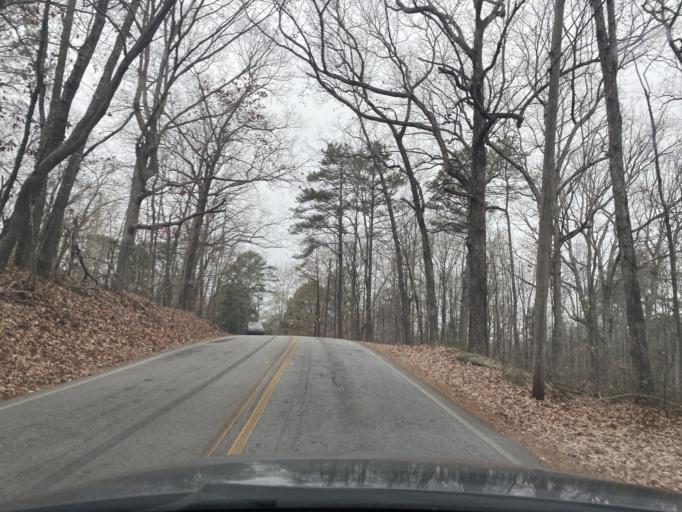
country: US
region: Georgia
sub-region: DeKalb County
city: Pine Mountain
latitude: 33.6841
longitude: -84.1462
